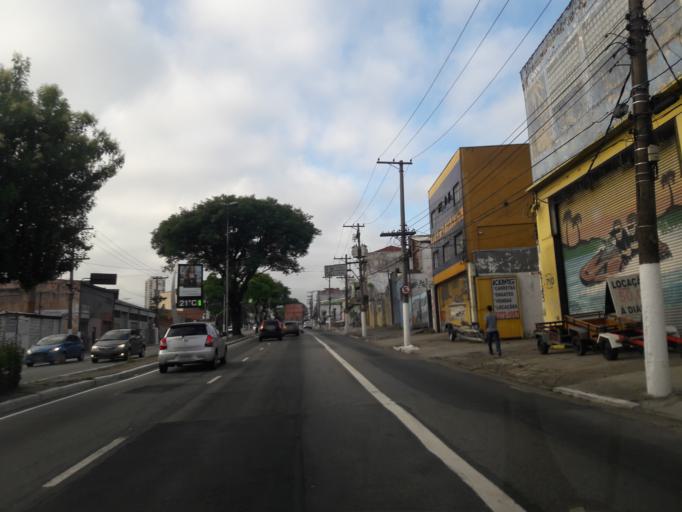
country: BR
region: Sao Paulo
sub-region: Sao Caetano Do Sul
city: Sao Caetano do Sul
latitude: -23.6079
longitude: -46.5995
